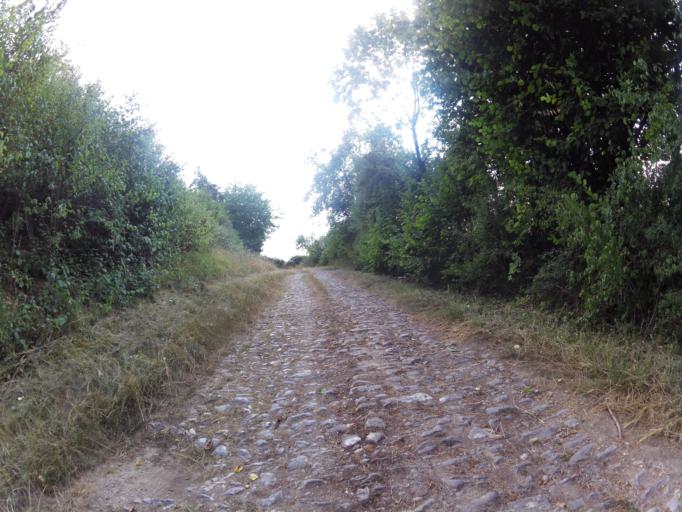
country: DE
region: Bavaria
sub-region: Regierungsbezirk Unterfranken
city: Ochsenfurt
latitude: 49.6580
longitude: 10.0696
